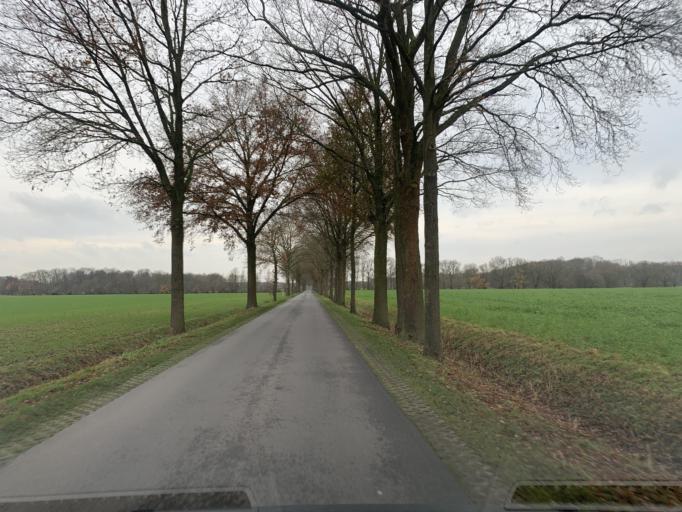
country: DE
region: North Rhine-Westphalia
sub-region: Regierungsbezirk Munster
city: Senden
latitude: 51.8910
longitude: 7.5566
